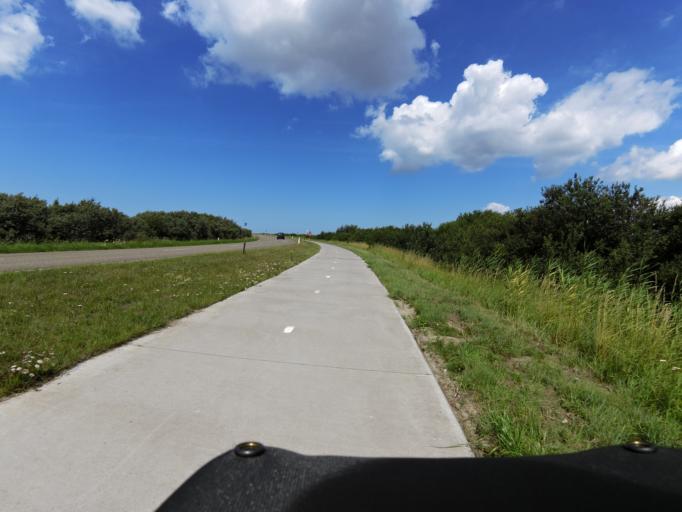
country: NL
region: South Holland
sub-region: Gemeente Goeree-Overflakkee
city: Ouddorp
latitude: 51.7901
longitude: 3.8858
